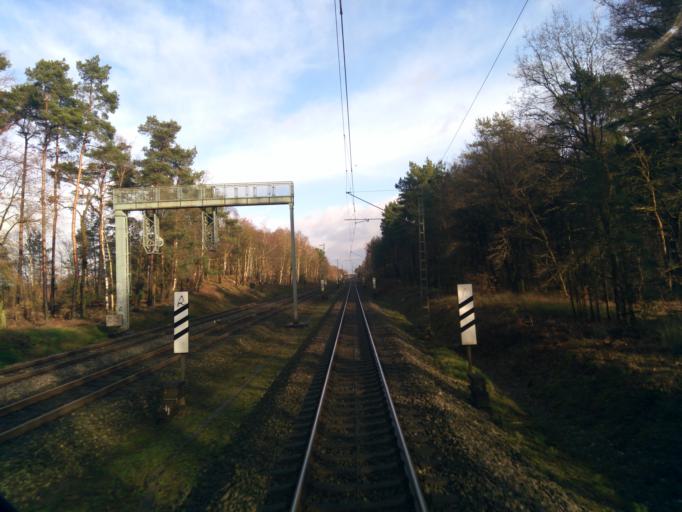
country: DE
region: Lower Saxony
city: Rotenburg
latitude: 53.1294
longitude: 9.4362
